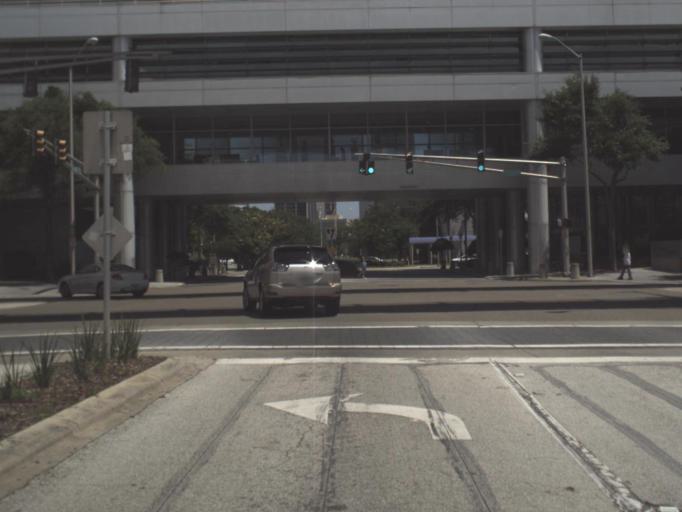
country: US
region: Florida
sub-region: Duval County
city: Jacksonville
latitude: 30.3175
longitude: -81.6604
